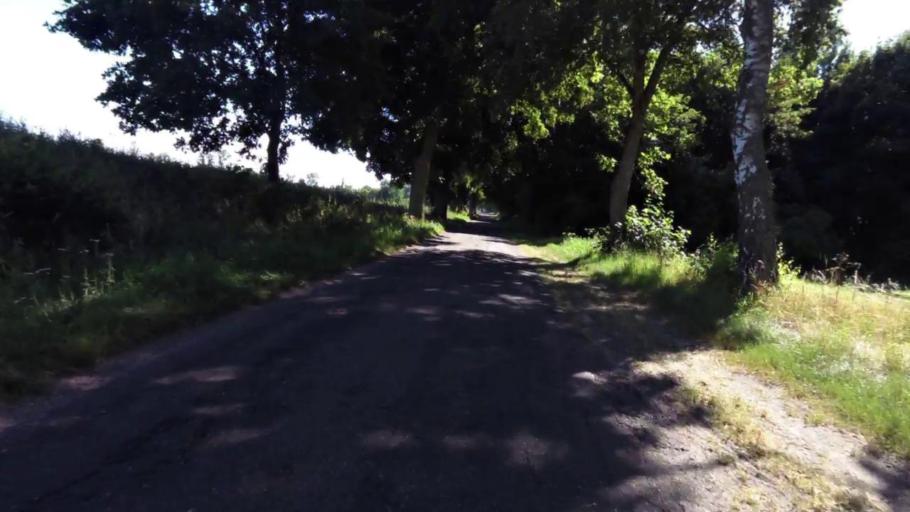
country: PL
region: West Pomeranian Voivodeship
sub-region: Powiat szczecinecki
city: Szczecinek
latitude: 53.7752
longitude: 16.6763
